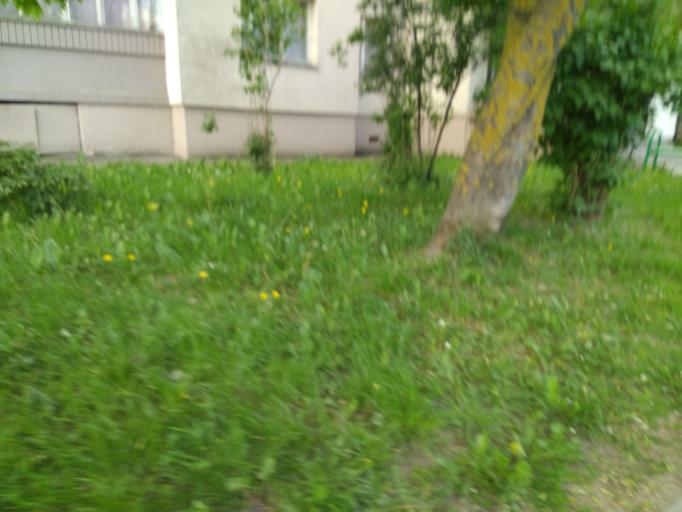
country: BY
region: Minsk
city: Minsk
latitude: 53.9104
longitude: 27.5353
